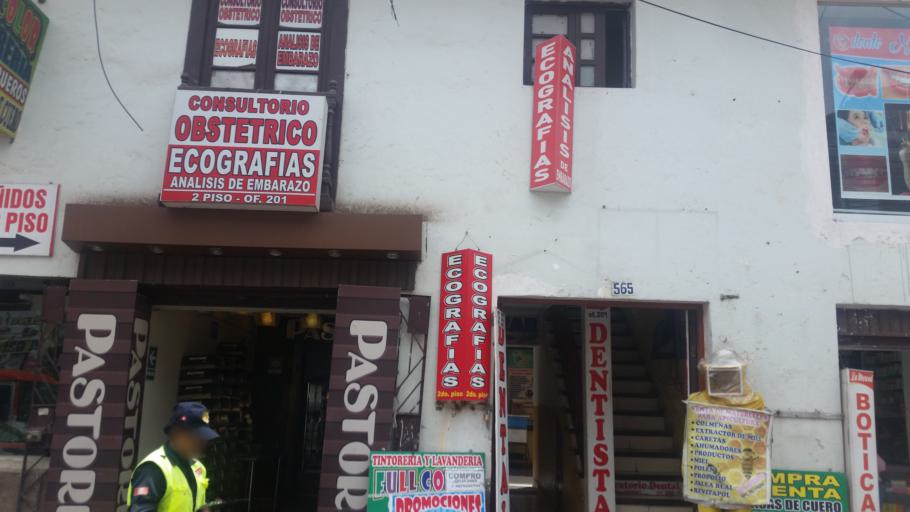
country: PE
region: Cusco
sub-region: Provincia de Cusco
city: Cusco
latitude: -13.5233
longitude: -71.9797
